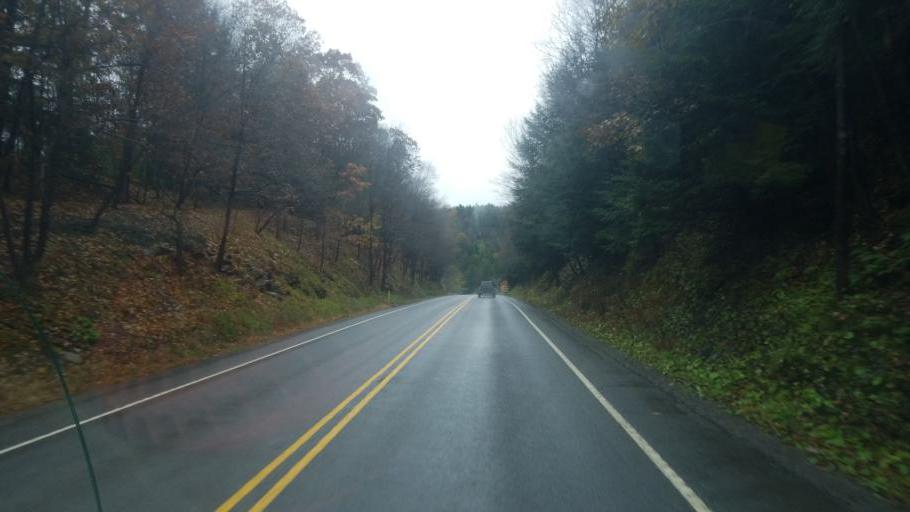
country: US
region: Pennsylvania
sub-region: Clearfield County
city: Shiloh
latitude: 41.0859
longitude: -78.2515
